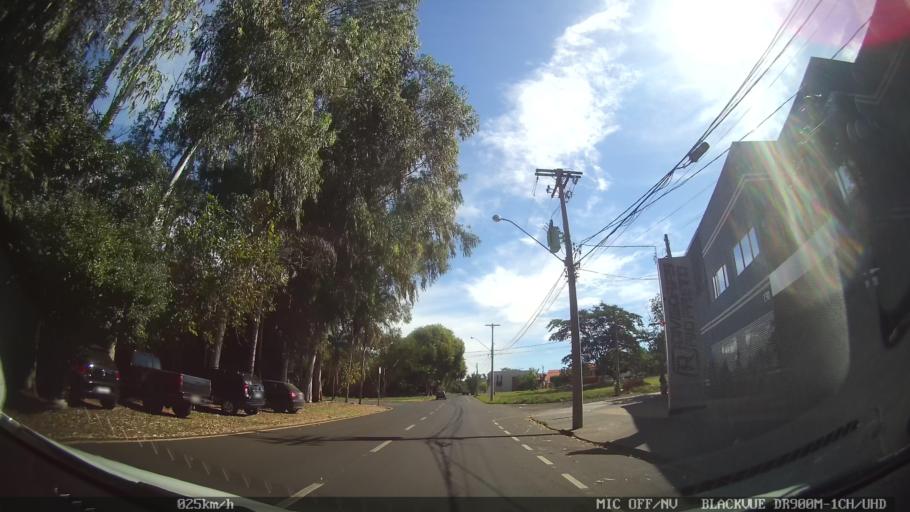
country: BR
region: Sao Paulo
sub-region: Sao Jose Do Rio Preto
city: Sao Jose do Rio Preto
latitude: -20.8435
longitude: -49.3597
